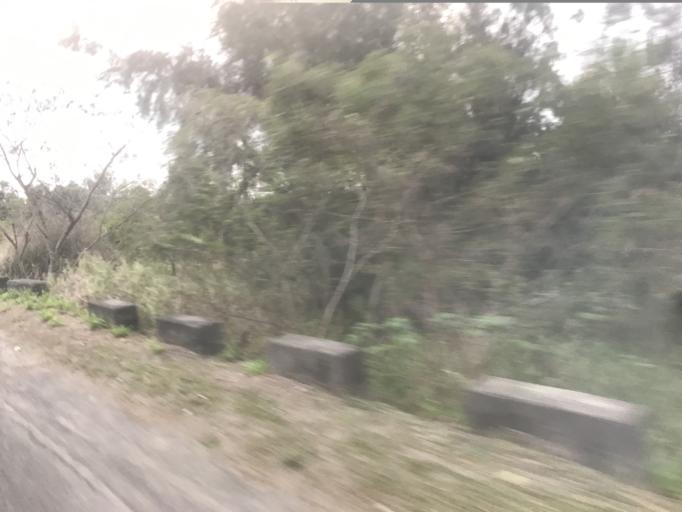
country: TW
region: Taiwan
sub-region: Hsinchu
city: Hsinchu
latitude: 24.7352
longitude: 120.8863
